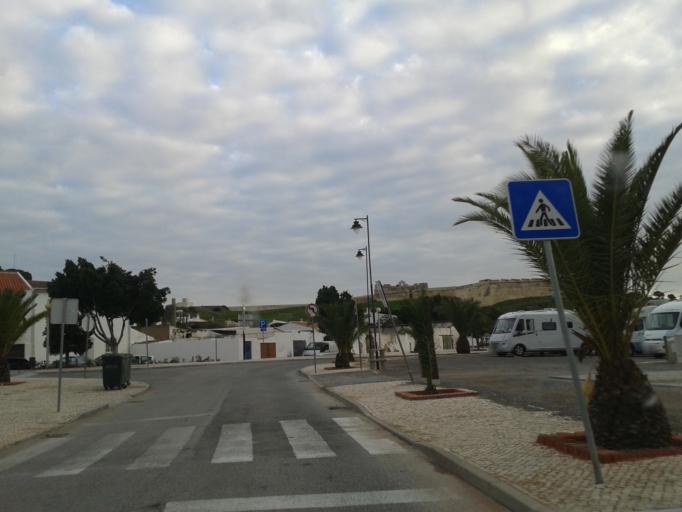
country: PT
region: Faro
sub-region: Castro Marim
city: Castro Marim
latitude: 37.2198
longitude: -7.4444
